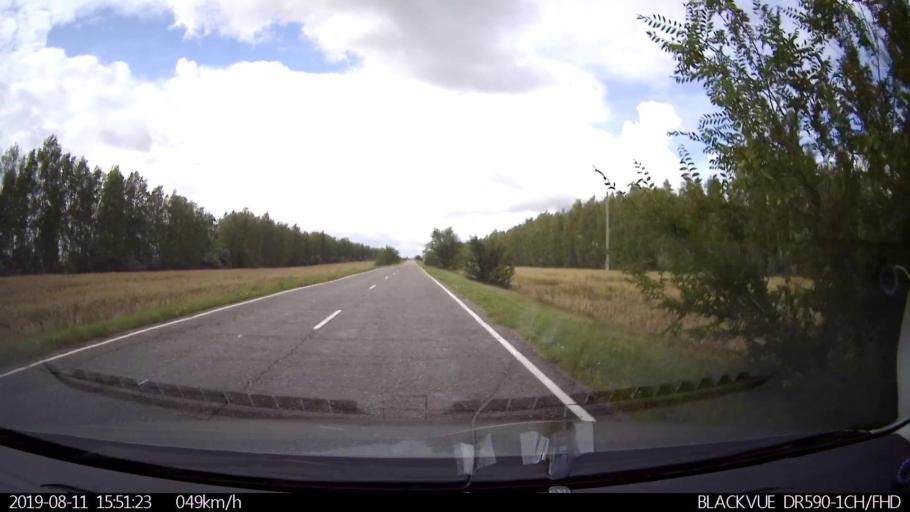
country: RU
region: Ulyanovsk
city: Ignatovka
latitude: 53.9184
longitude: 47.6560
